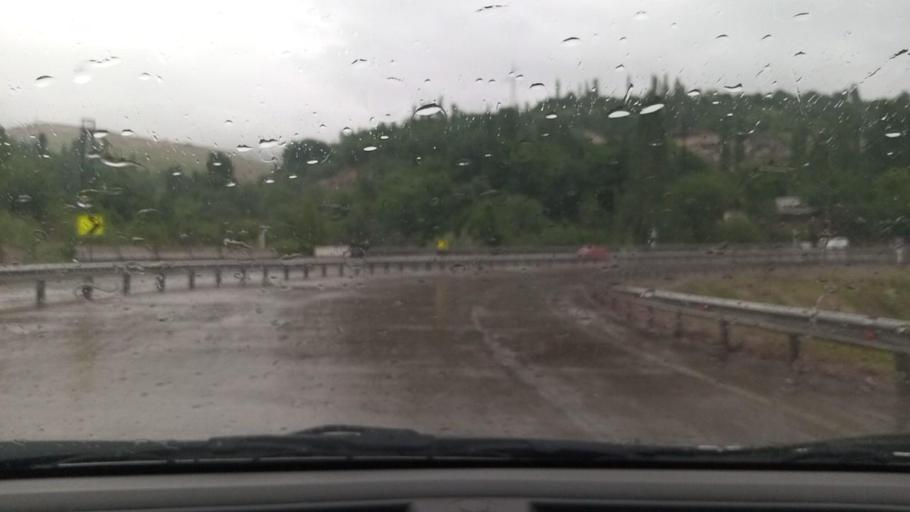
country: UZ
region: Toshkent
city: Angren
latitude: 41.0746
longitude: 70.2519
